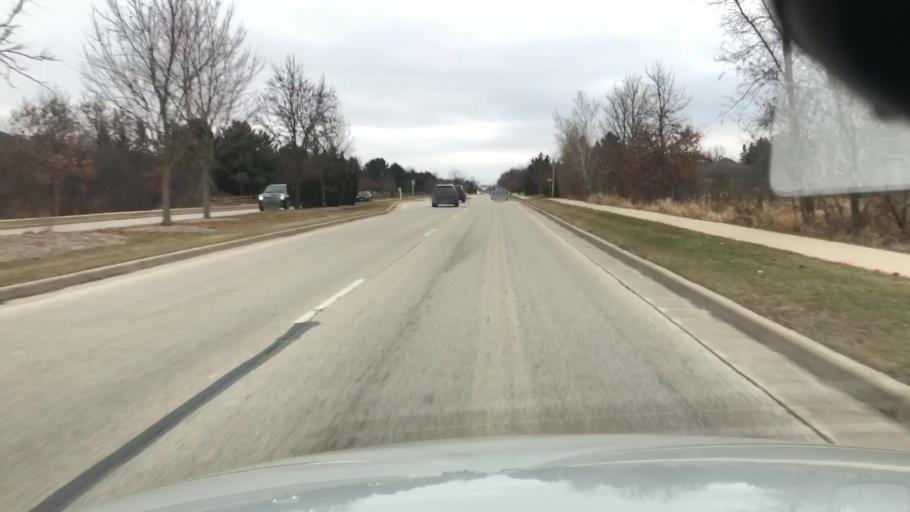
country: US
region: Wisconsin
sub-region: Waukesha County
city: Brookfield
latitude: 43.0434
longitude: -88.1268
